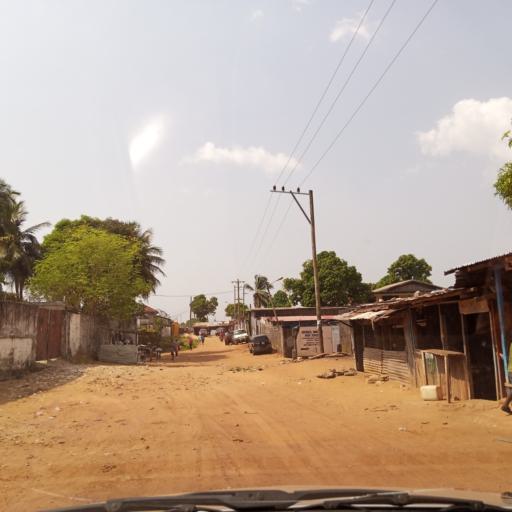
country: LR
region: Montserrado
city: Monrovia
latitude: 6.2900
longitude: -10.7651
